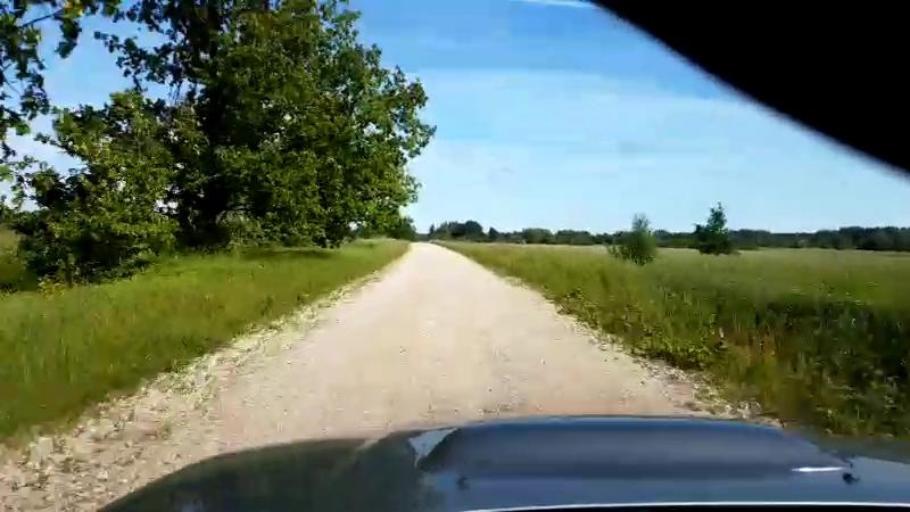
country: EE
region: Paernumaa
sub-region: Sauga vald
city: Sauga
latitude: 58.4786
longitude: 24.5318
